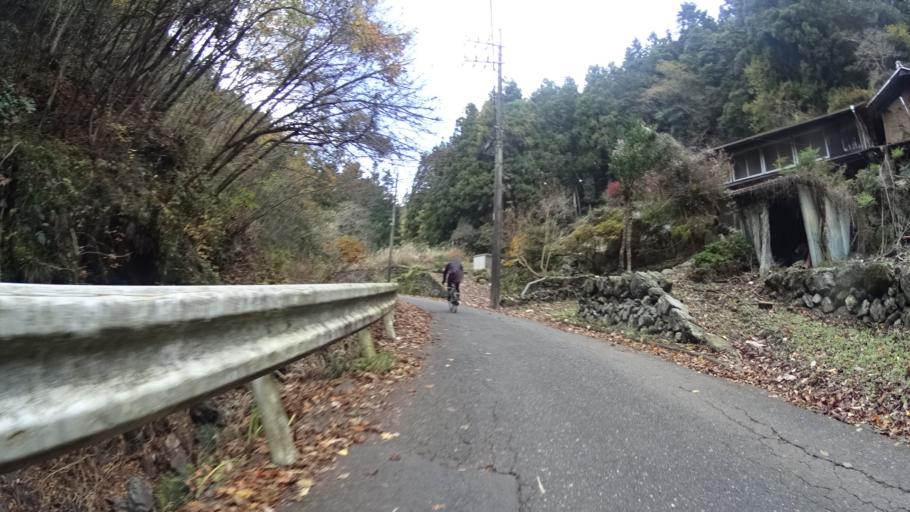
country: JP
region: Saitama
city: Morohongo
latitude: 35.9095
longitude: 139.2032
